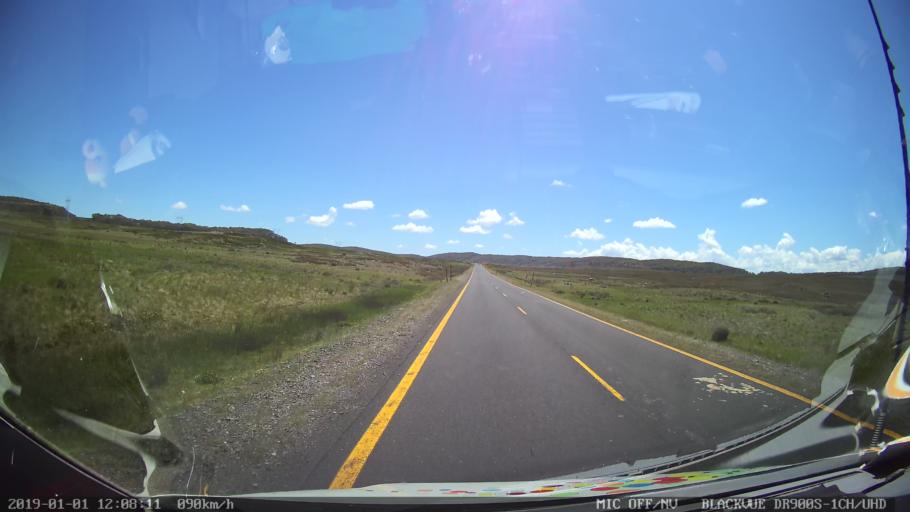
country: AU
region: New South Wales
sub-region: Tumut Shire
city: Tumut
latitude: -35.8236
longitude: 148.4935
